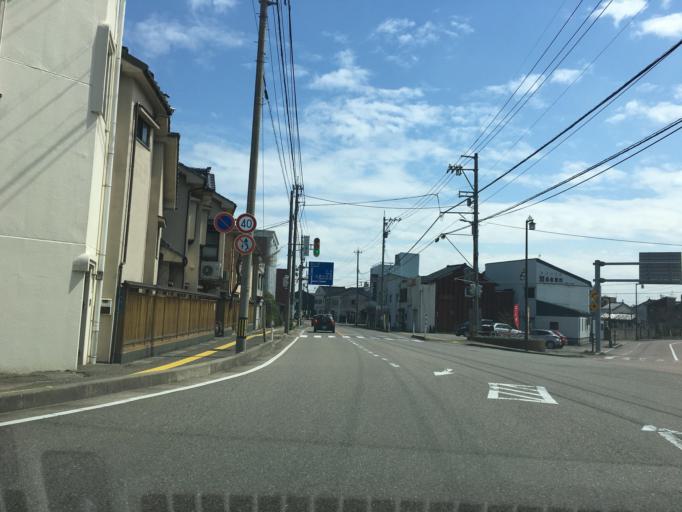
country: JP
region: Toyama
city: Nishishinminato
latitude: 36.7795
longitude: 137.0859
